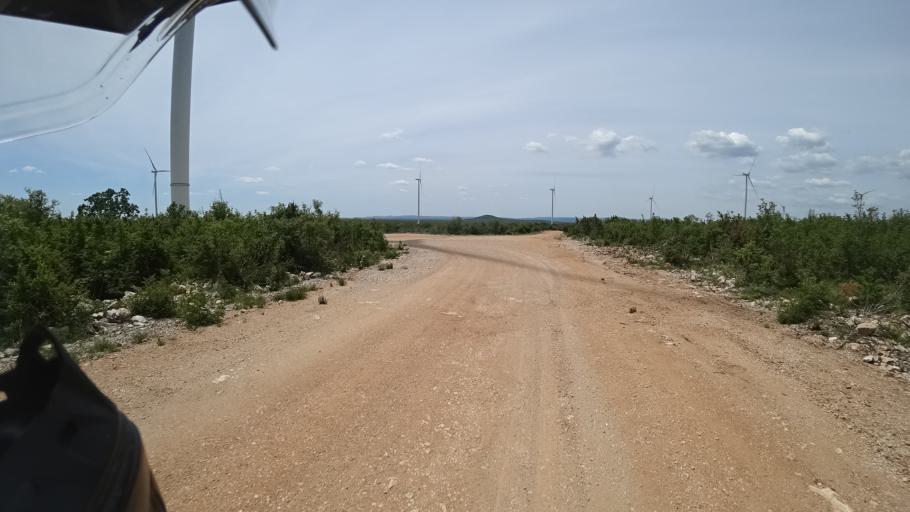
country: HR
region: Sibensko-Kniniska
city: Knin
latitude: 44.0601
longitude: 16.0856
